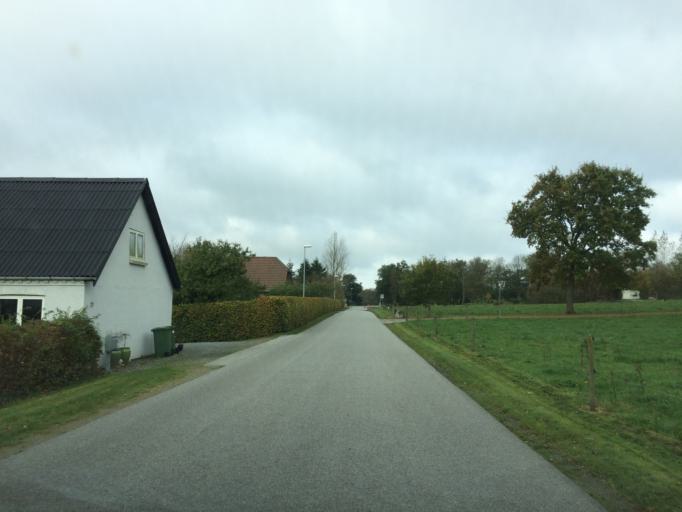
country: DK
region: Central Jutland
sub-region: Holstebro Kommune
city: Holstebro
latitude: 56.3338
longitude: 8.4888
